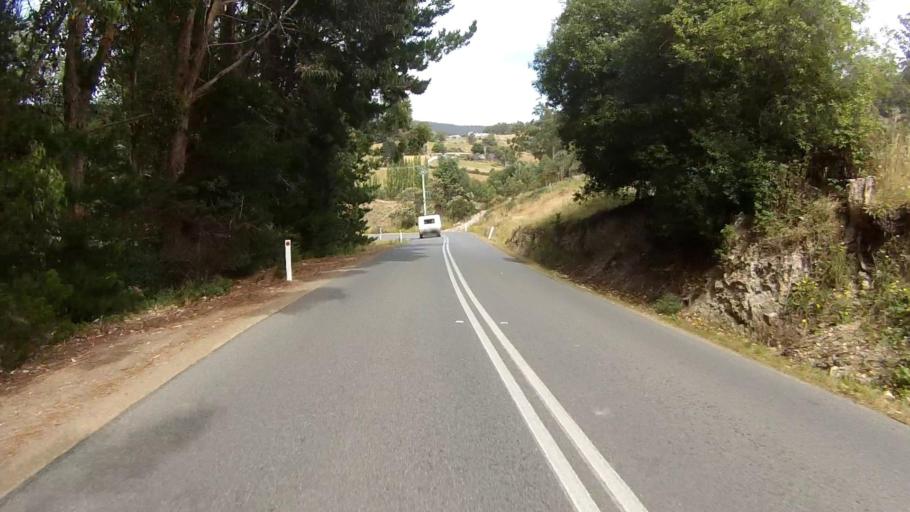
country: AU
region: Tasmania
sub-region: Kingborough
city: Kettering
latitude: -43.1749
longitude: 147.2369
